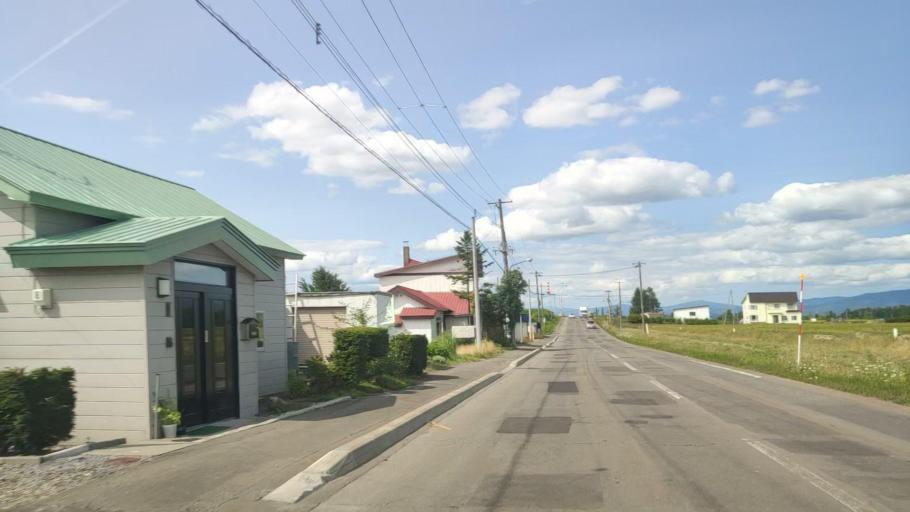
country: JP
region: Hokkaido
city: Nayoro
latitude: 44.2969
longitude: 142.4294
